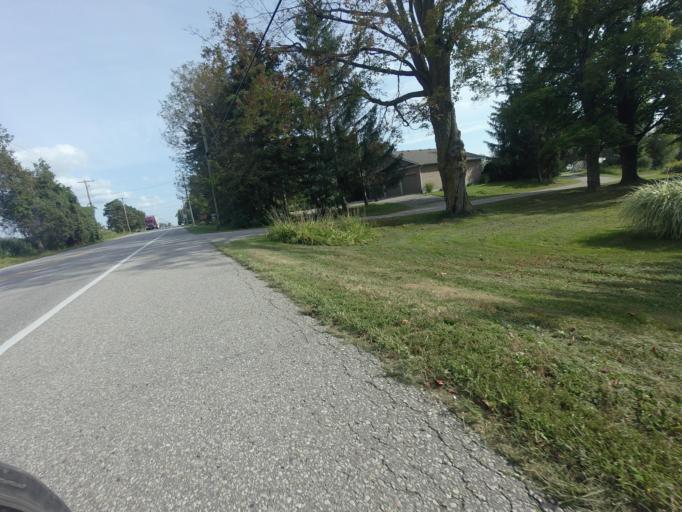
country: CA
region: Ontario
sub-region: Wellington County
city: Guelph
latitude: 43.5591
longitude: -80.3070
